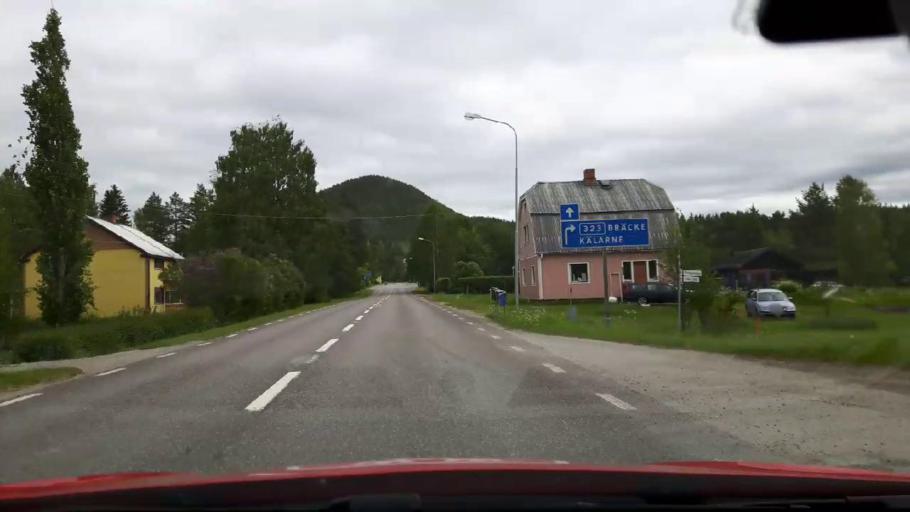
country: SE
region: Jaemtland
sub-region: Ragunda Kommun
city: Hammarstrand
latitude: 63.0617
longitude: 16.3959
